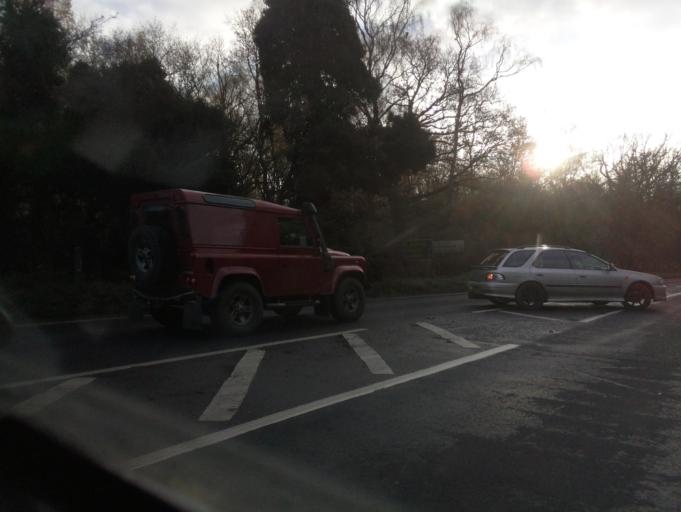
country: GB
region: England
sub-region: City and Borough of Birmingham
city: Sutton Coldfield
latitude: 52.5902
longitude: -1.7809
